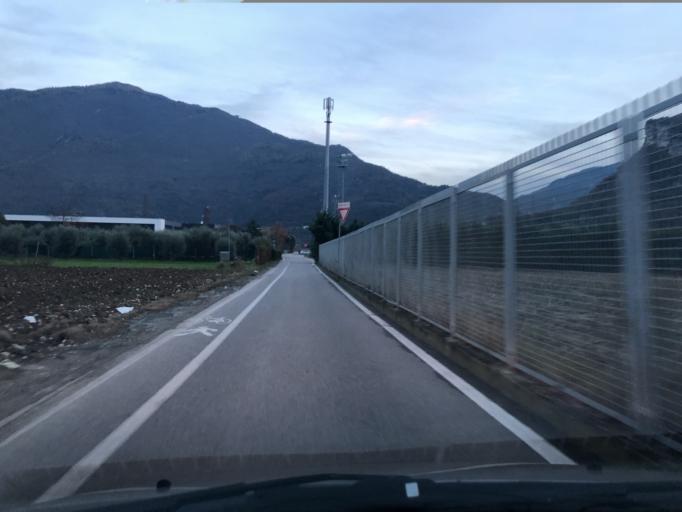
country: IT
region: Trentino-Alto Adige
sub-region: Provincia di Trento
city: Arco
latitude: 45.9020
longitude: 10.8687
